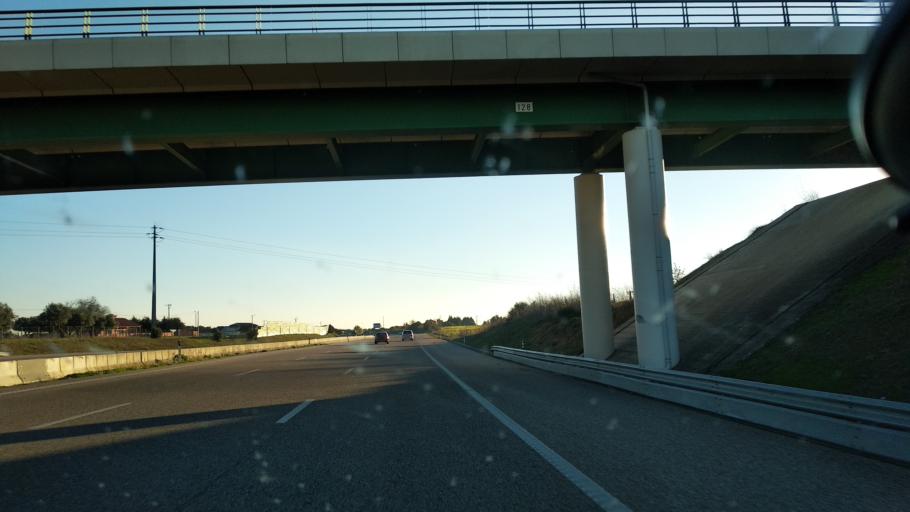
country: PT
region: Santarem
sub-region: Alcanena
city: Alcanena
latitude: 39.4020
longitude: -8.6381
